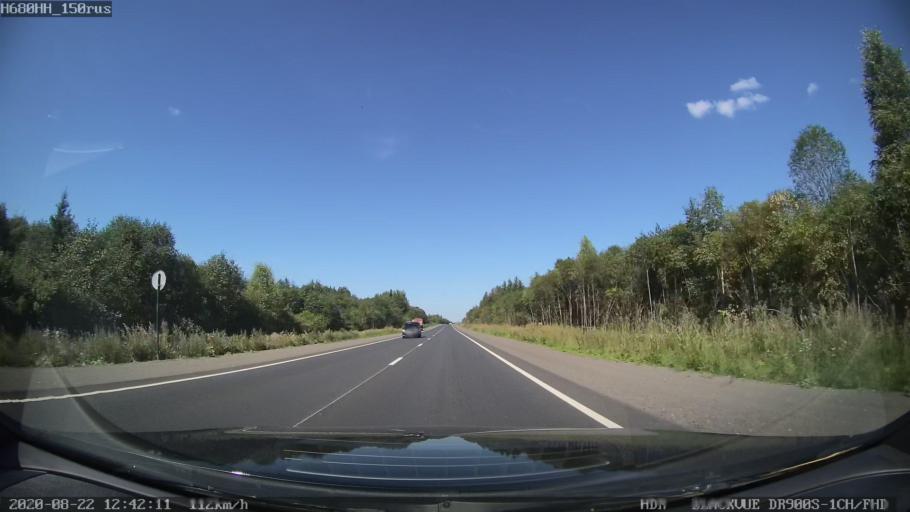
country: RU
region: Tverskaya
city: Rameshki
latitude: 57.3582
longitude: 36.0955
